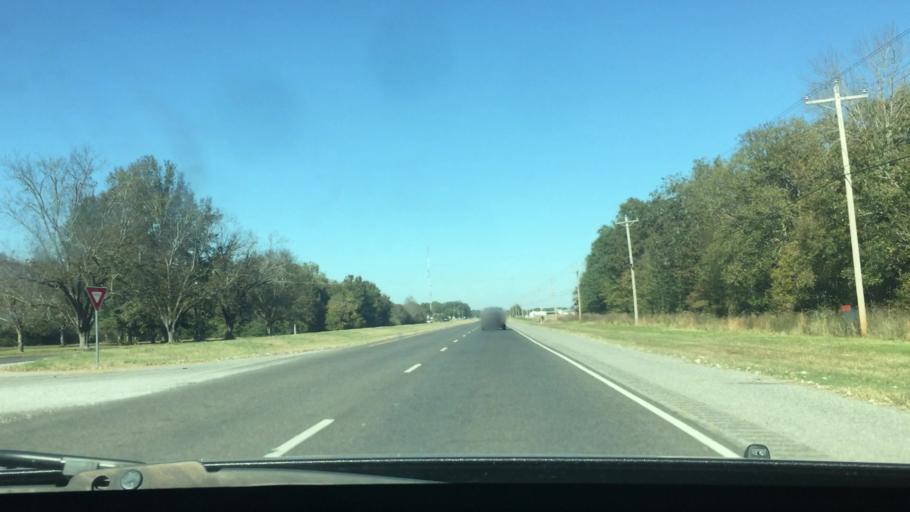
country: US
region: Louisiana
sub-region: Richland Parish
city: Rayville
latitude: 32.4101
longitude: -91.7662
